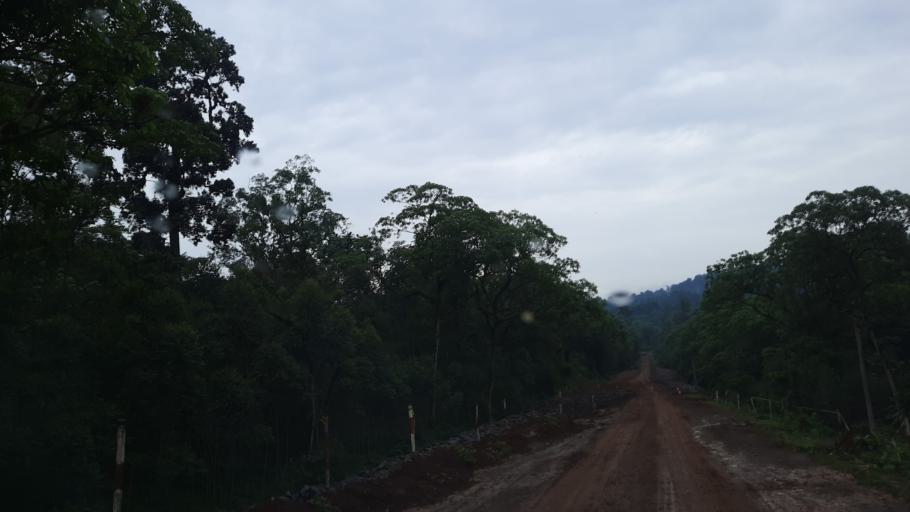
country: ET
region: Oromiya
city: Gore
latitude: 7.8674
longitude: 35.4801
